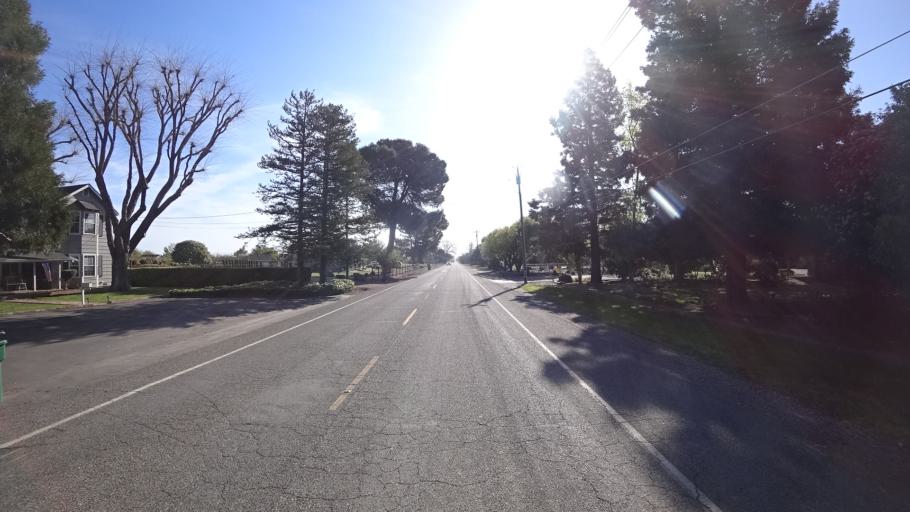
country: US
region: California
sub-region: Glenn County
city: Willows
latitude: 39.5388
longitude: -122.2009
